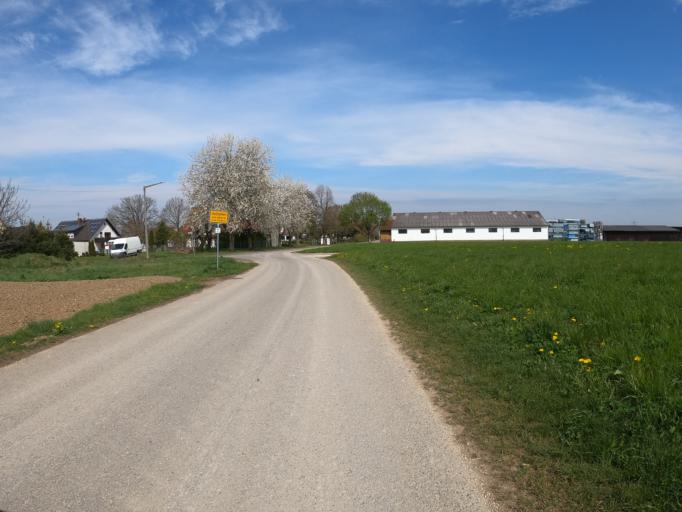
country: DE
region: Bavaria
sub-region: Swabia
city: Rieden an der Kotz
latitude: 48.3821
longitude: 10.2177
